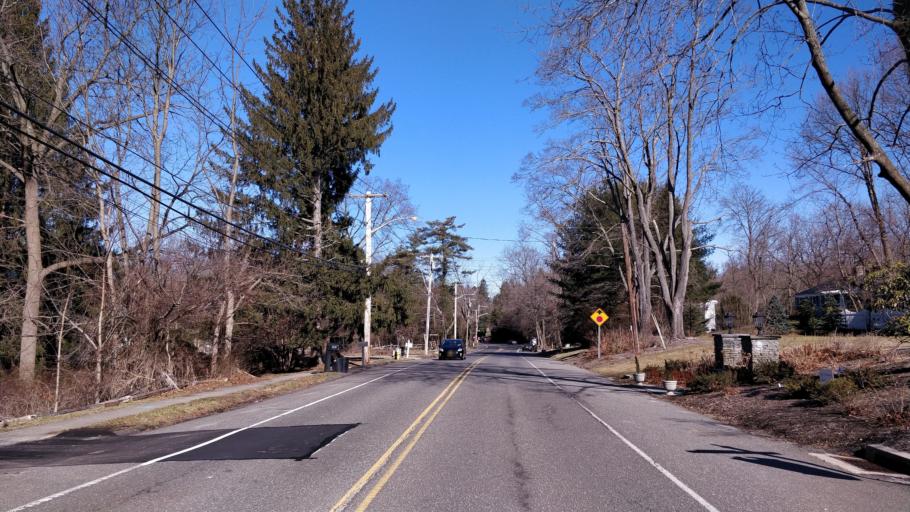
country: US
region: New York
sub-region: Suffolk County
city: Setauket-East Setauket
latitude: 40.9340
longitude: -73.1003
